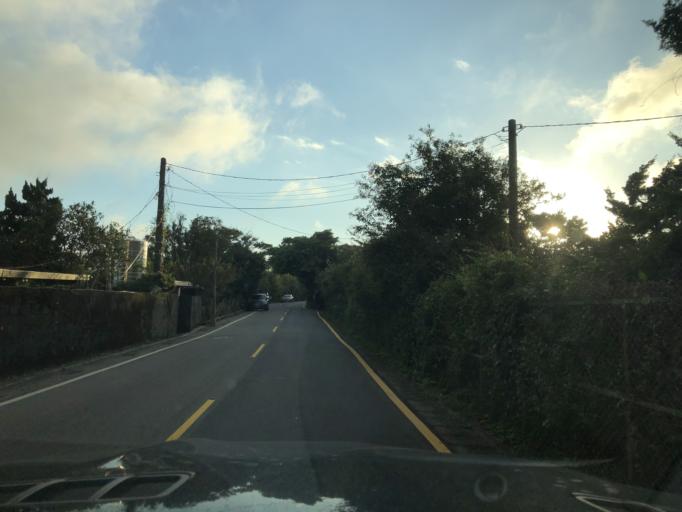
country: TW
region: Taipei
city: Taipei
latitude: 25.1500
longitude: 121.5608
